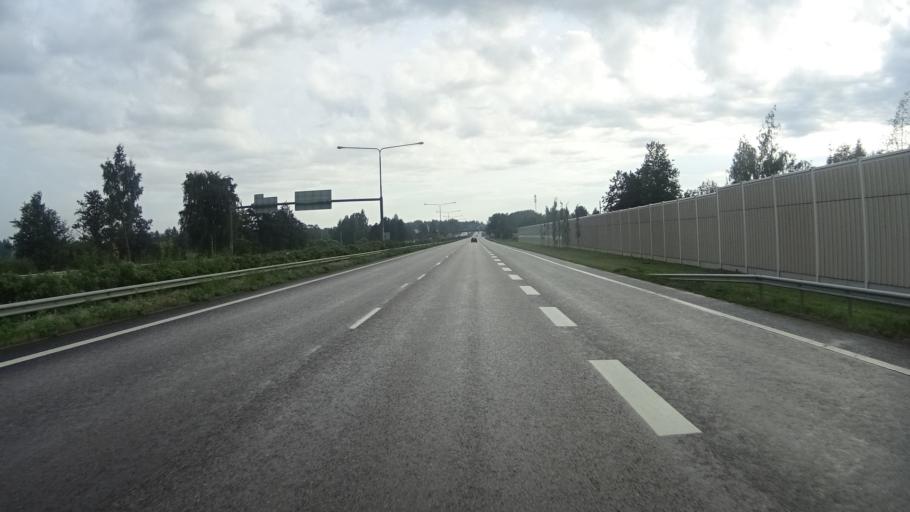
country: FI
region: Kymenlaakso
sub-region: Kotka-Hamina
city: Karhula
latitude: 60.5267
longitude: 26.9539
